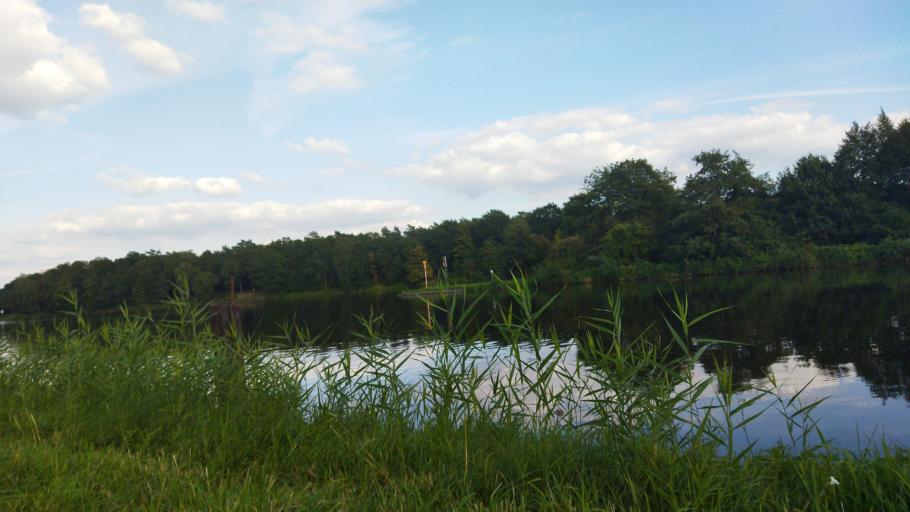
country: DE
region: Lower Saxony
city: Dersum
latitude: 52.9586
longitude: 7.2980
